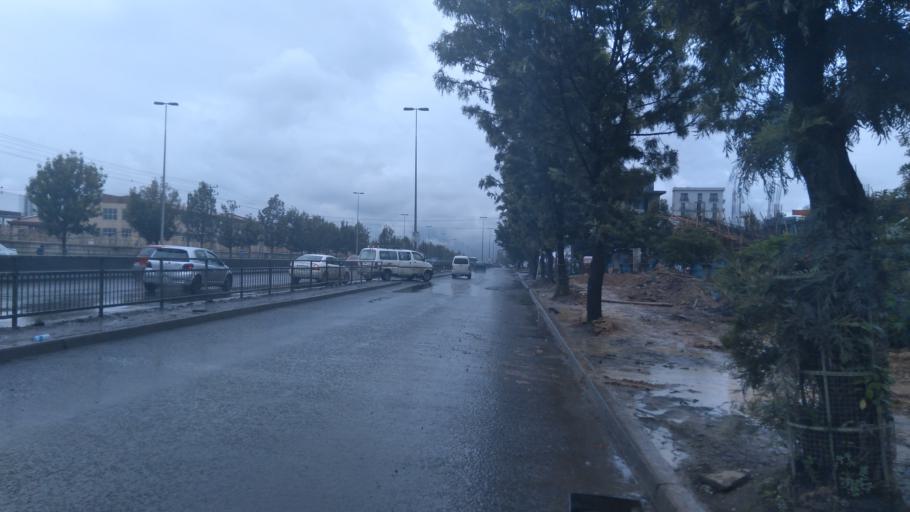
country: ET
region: Adis Abeba
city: Addis Ababa
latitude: 8.9852
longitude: 38.7863
